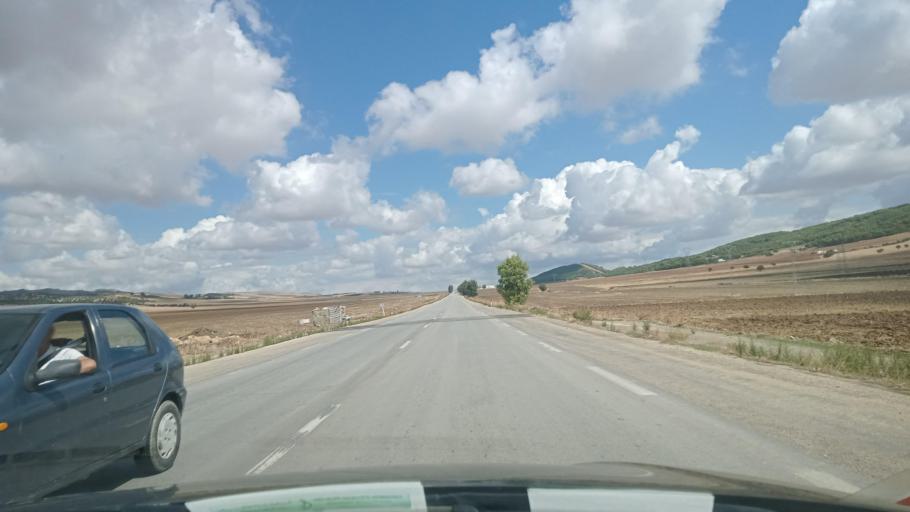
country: TN
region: Silyanah
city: Al Karib
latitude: 36.3061
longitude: 9.0908
